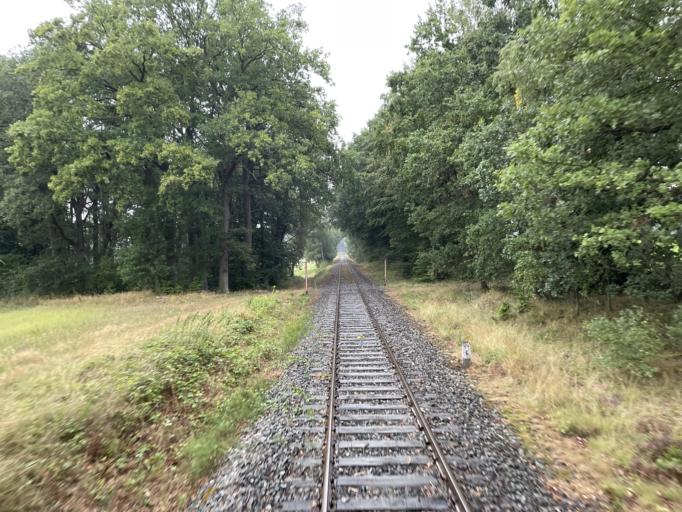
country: DE
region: Lower Saxony
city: Embsen
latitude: 53.1631
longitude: 10.3547
